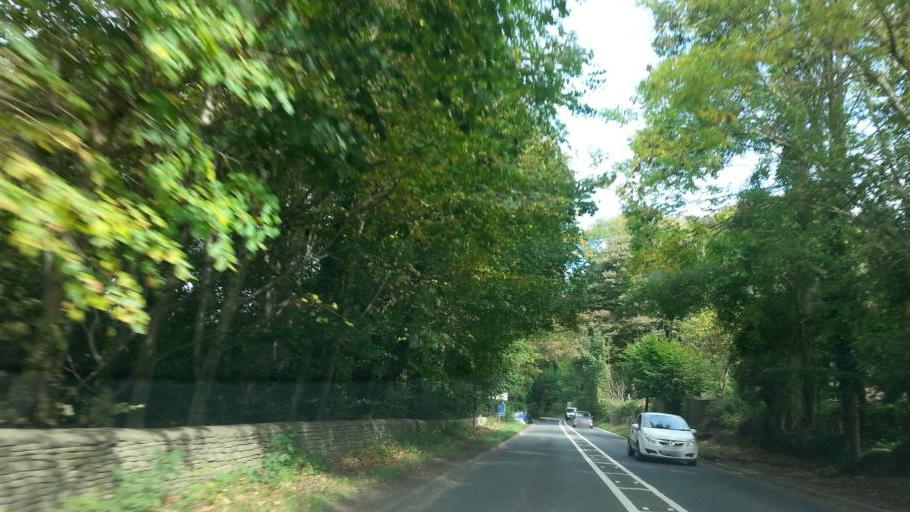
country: GB
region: England
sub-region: Gloucestershire
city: Painswick
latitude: 51.8159
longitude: -2.1725
